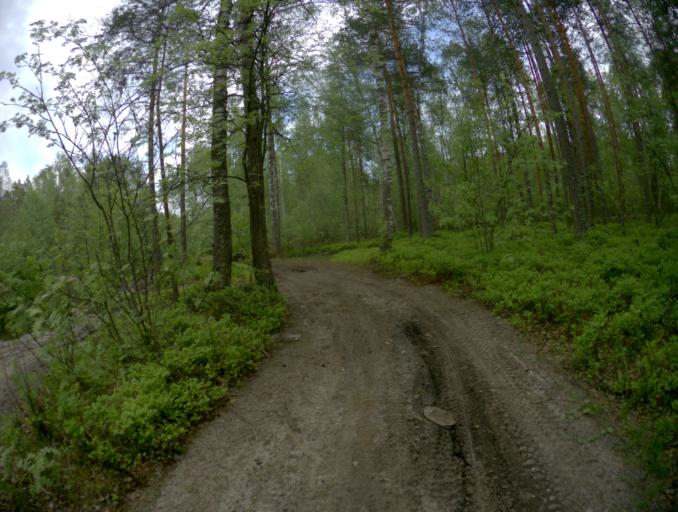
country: RU
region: Vladimir
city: Ivanishchi
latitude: 55.7586
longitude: 40.3999
